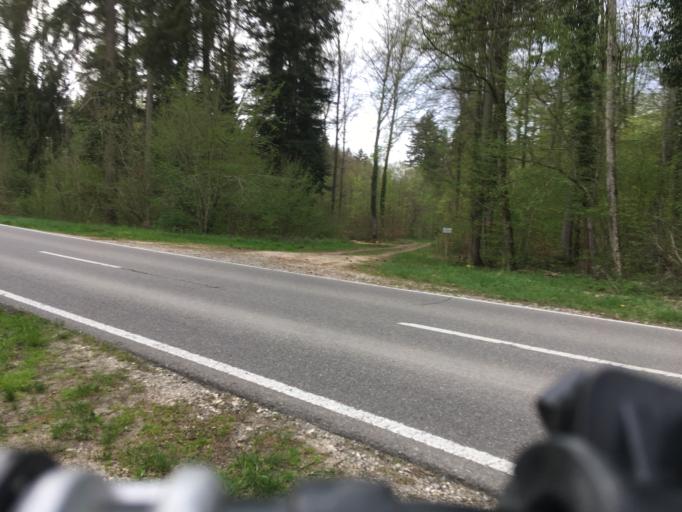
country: DE
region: Baden-Wuerttemberg
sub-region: Freiburg Region
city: Gailingen
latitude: 47.7172
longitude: 8.7370
